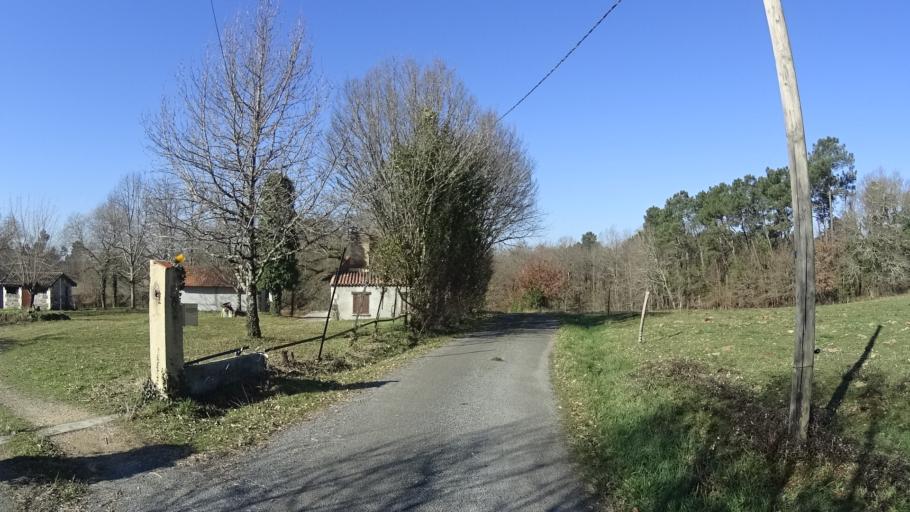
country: FR
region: Aquitaine
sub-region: Departement de la Dordogne
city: Montpon-Menesterol
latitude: 45.0459
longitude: 0.2464
